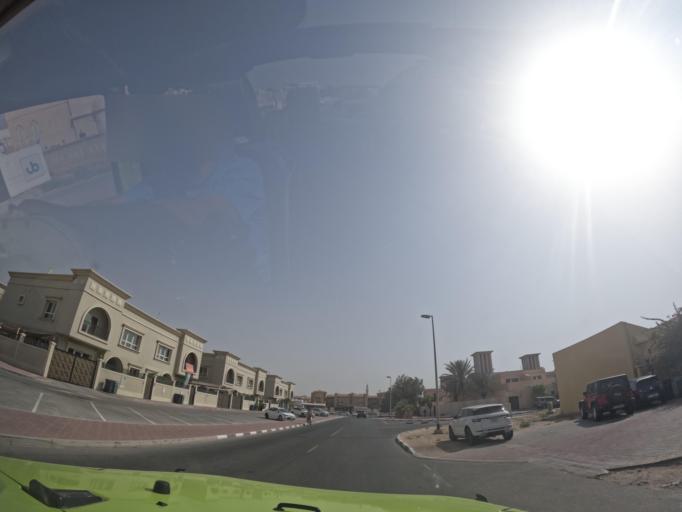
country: AE
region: Dubai
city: Dubai
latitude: 25.1479
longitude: 55.2146
